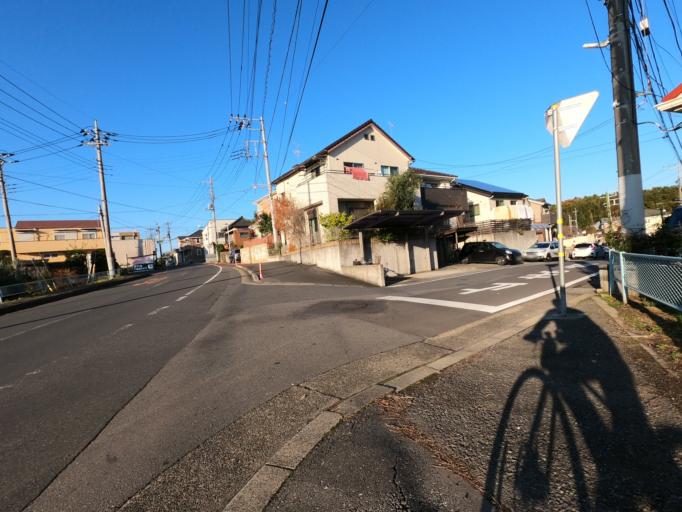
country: JP
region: Ibaraki
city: Moriya
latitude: 35.9432
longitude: 139.9992
